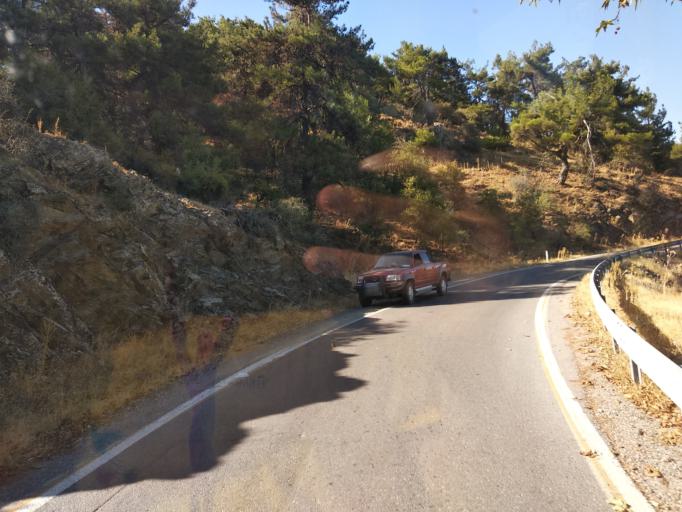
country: TR
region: Izmir
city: Gaziemir
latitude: 38.3220
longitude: 27.0066
